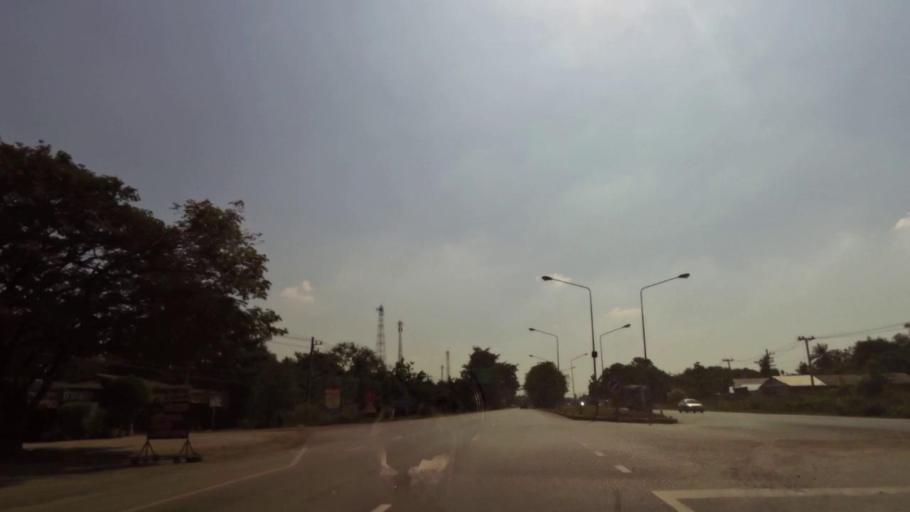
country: TH
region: Phichit
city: Bueng Na Rang
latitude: 16.1937
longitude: 100.1286
